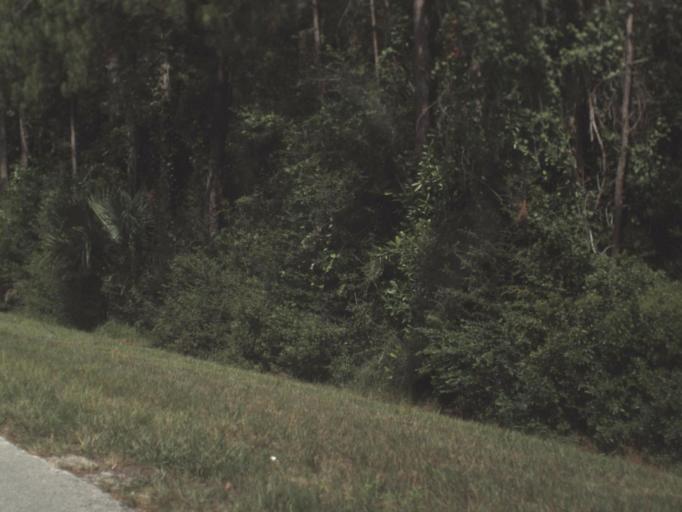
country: US
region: Florida
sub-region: Baker County
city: Macclenny
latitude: 30.2370
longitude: -82.1386
